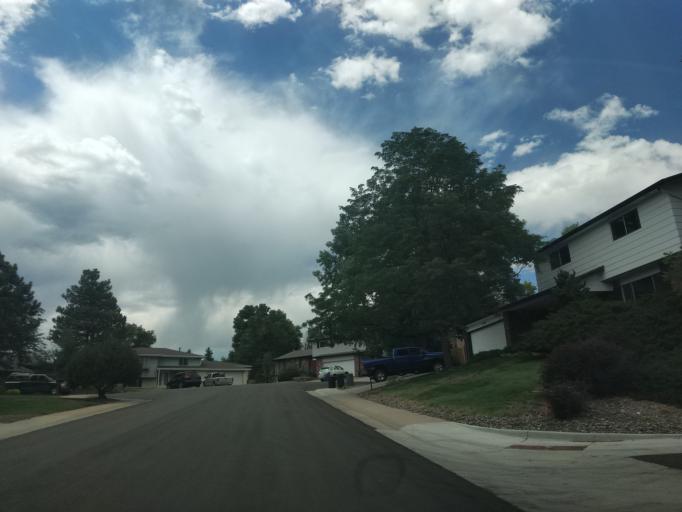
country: US
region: Colorado
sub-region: Jefferson County
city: Lakewood
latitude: 39.6738
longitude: -105.1040
